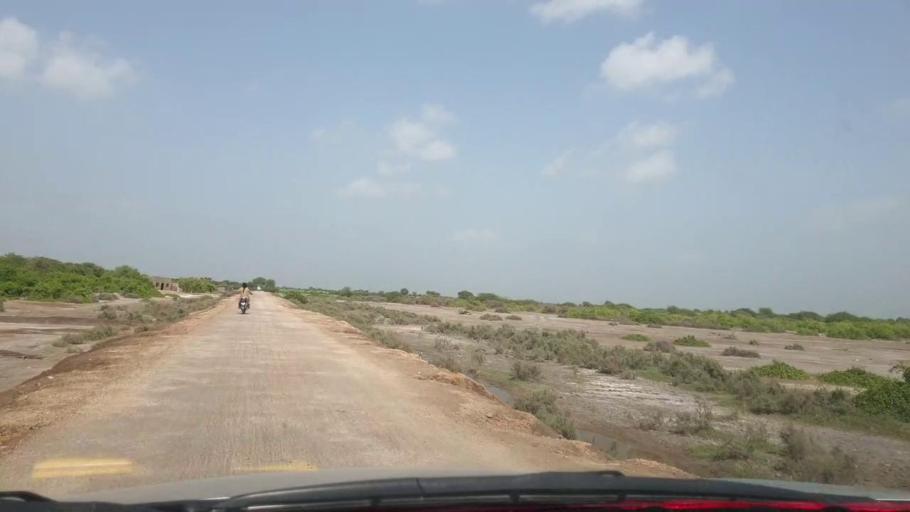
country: PK
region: Sindh
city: Tando Bago
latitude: 24.8757
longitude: 68.9295
